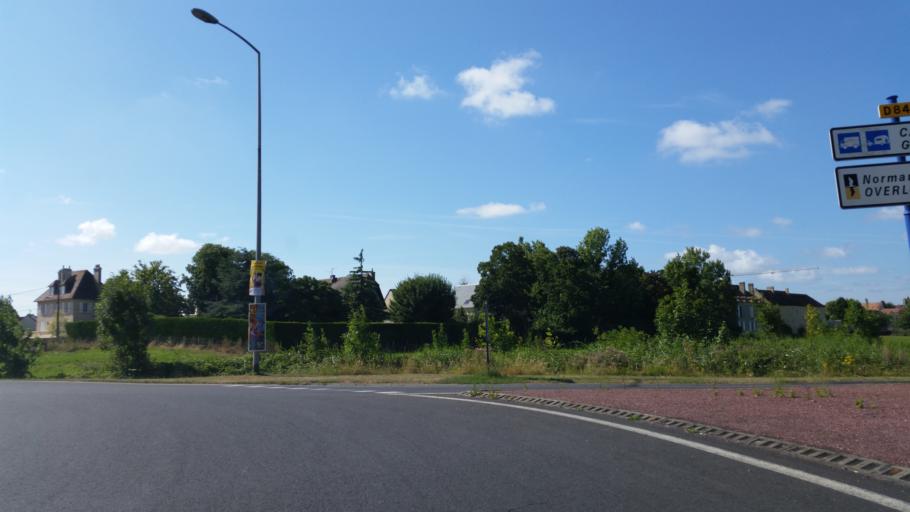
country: FR
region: Lower Normandy
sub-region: Departement du Calvados
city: Ouistreham
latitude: 49.2709
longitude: -0.2551
